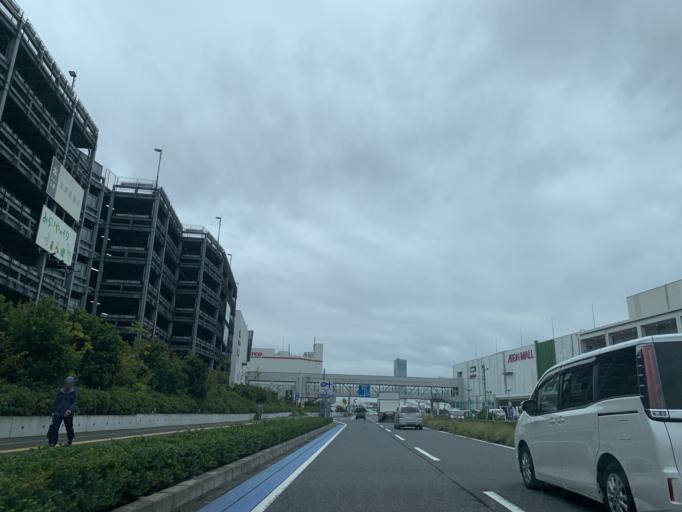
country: JP
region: Chiba
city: Funabashi
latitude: 35.6568
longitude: 140.0250
